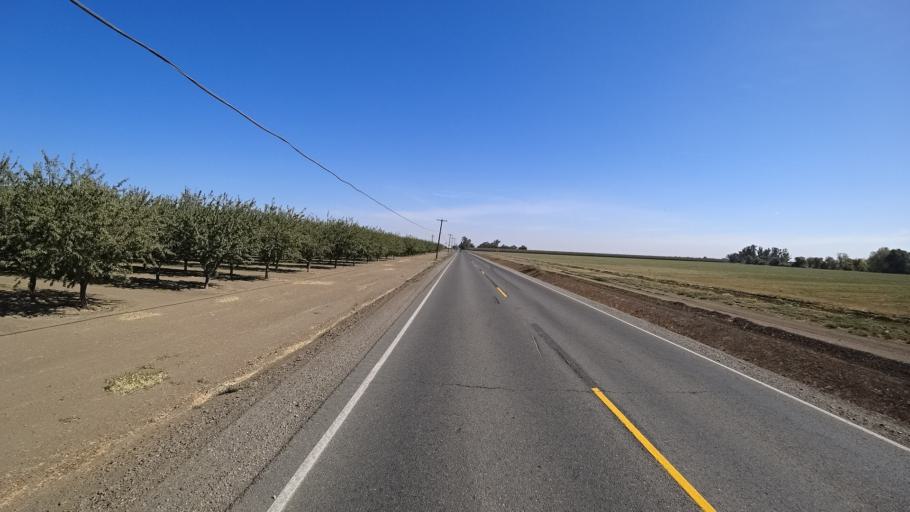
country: US
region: California
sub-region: Yolo County
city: Woodland
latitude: 38.6196
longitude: -121.8279
